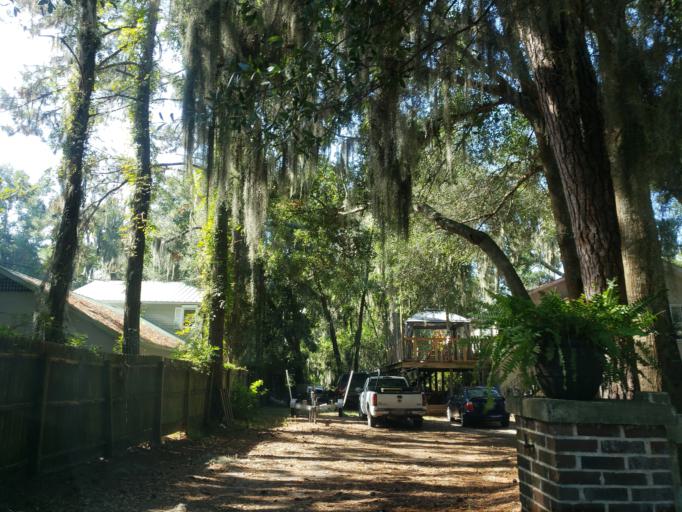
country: US
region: Georgia
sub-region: Chatham County
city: Montgomery
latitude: 31.9379
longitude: -81.1056
